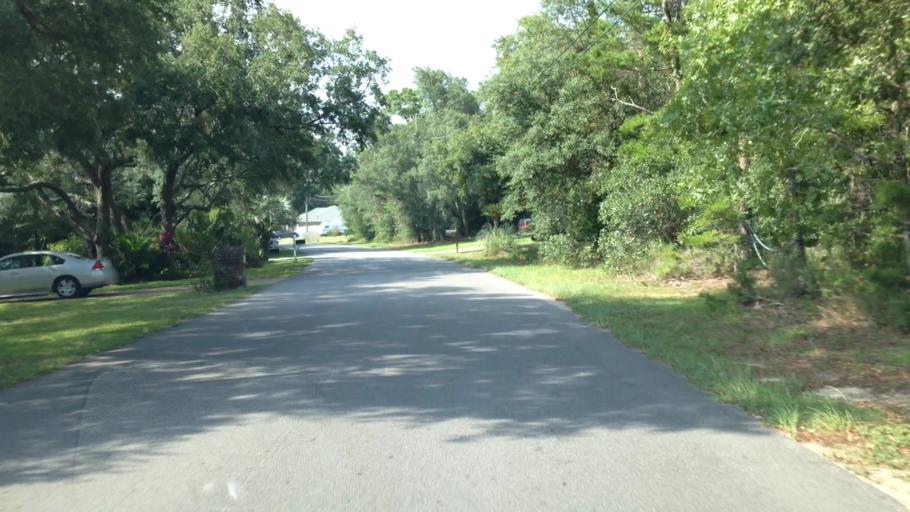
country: US
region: Florida
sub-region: Santa Rosa County
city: Holley
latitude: 30.4382
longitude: -86.9346
